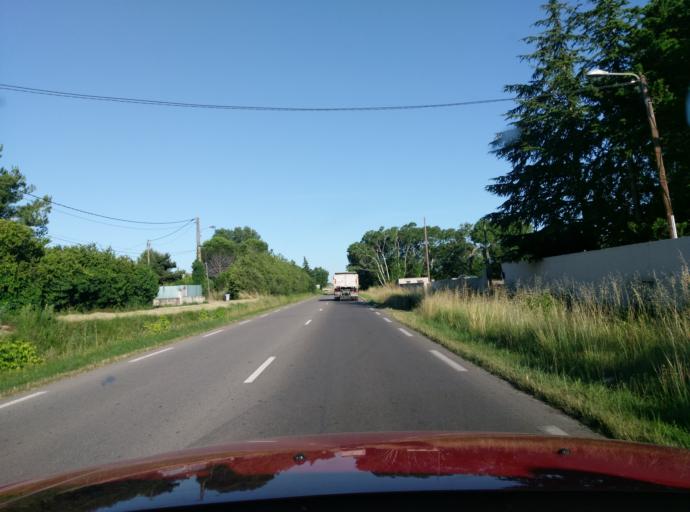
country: FR
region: Languedoc-Roussillon
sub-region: Departement du Gard
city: Redessan
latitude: 43.8273
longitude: 4.4845
